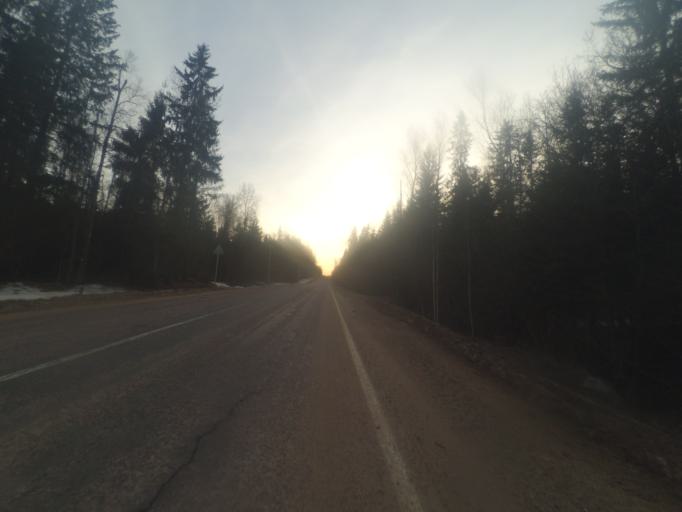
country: RU
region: Moskovskaya
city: Karinskoye
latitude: 55.7805
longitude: 36.6272
